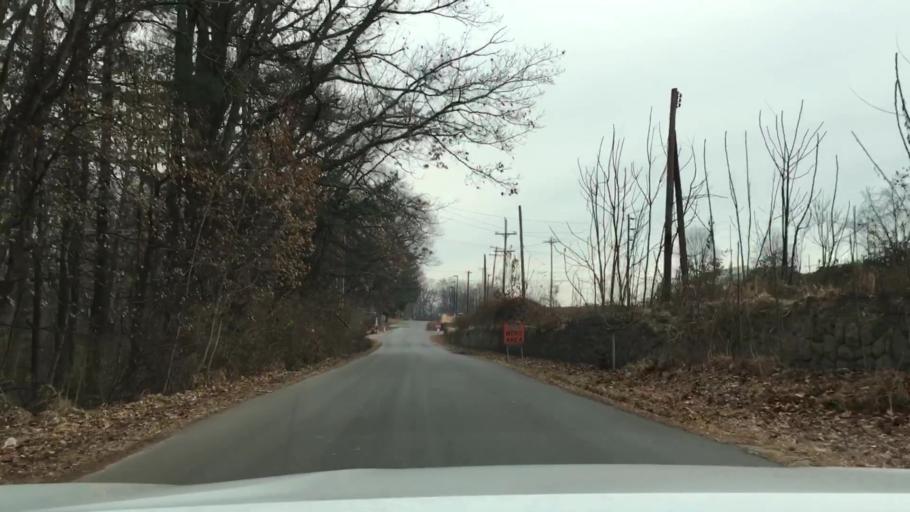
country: US
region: Pennsylvania
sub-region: Chester County
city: Spring City
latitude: 40.1917
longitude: -75.5689
